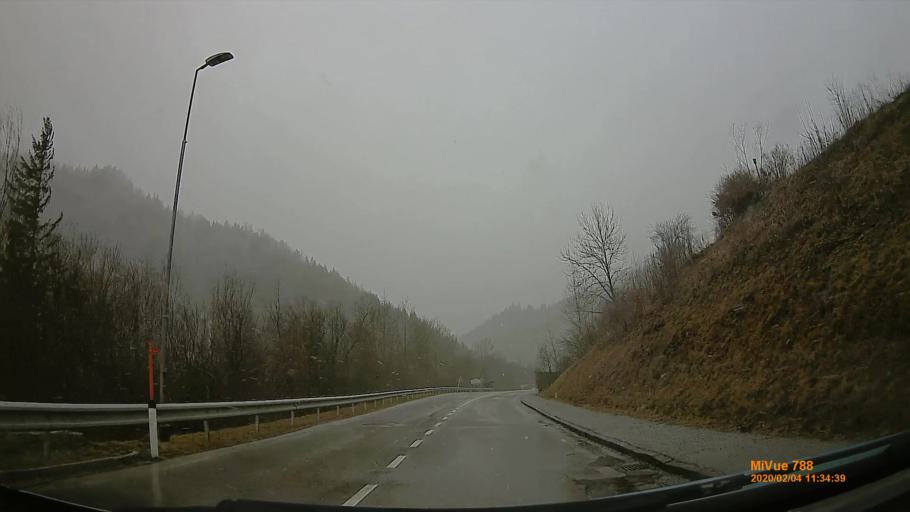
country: AT
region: Styria
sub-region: Politischer Bezirk Bruck-Muerzzuschlag
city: Neuberg an der Muerz
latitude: 47.6705
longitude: 15.5712
